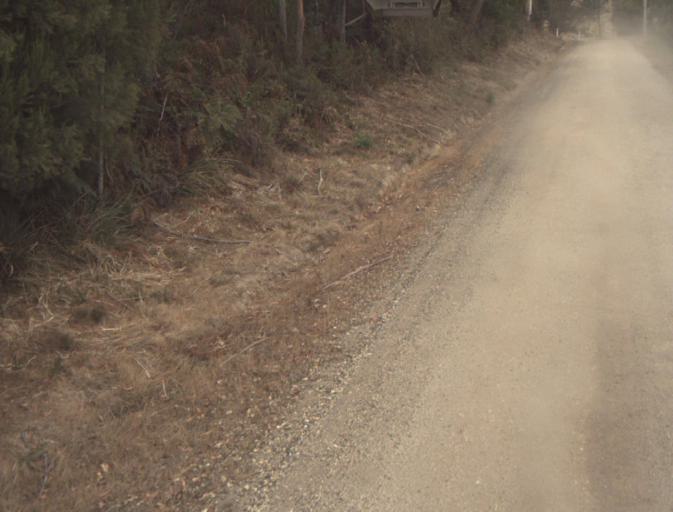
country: AU
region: Tasmania
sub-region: Dorset
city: Bridport
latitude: -41.1787
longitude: 147.2618
